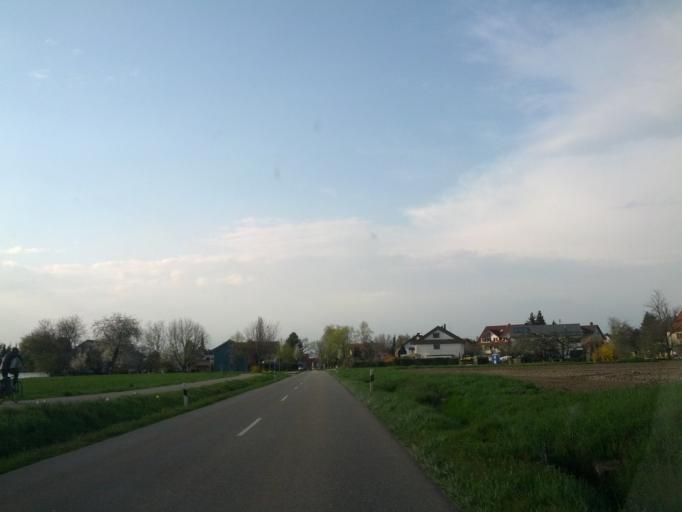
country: DE
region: Baden-Wuerttemberg
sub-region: Freiburg Region
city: Vorstetten
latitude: 48.0589
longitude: 7.8544
